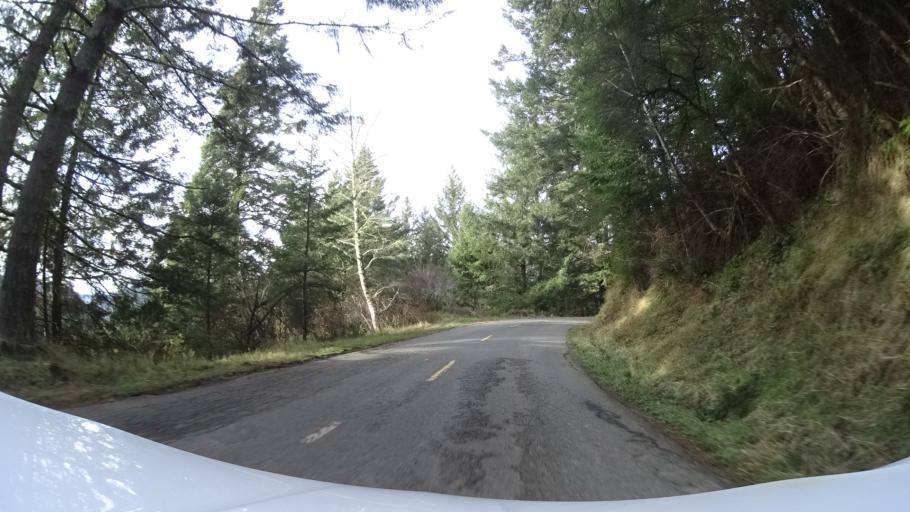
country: US
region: California
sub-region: Humboldt County
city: Ferndale
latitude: 40.5274
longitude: -124.2696
